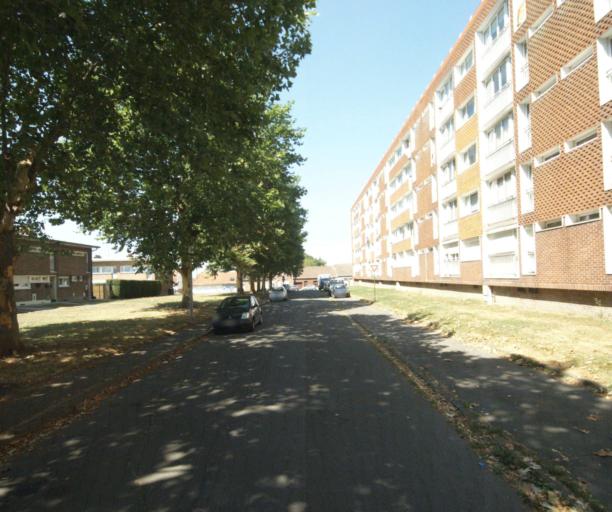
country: FR
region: Nord-Pas-de-Calais
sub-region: Departement du Nord
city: Wattrelos
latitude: 50.7074
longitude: 3.2285
